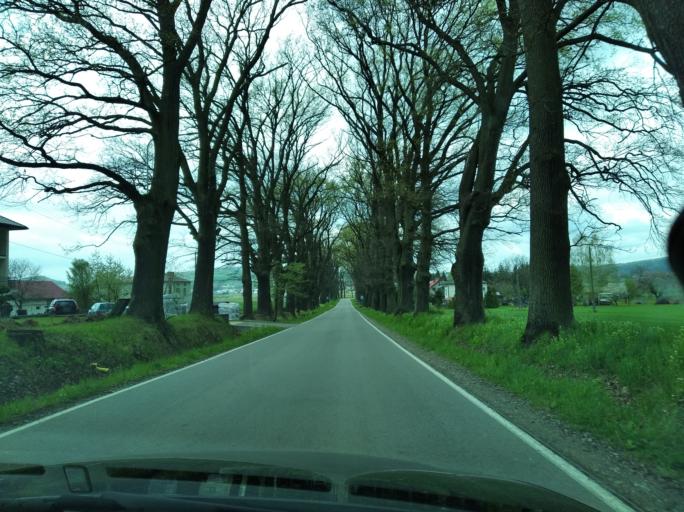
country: PL
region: Subcarpathian Voivodeship
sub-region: Powiat brzozowski
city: Turze Pole
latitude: 49.6456
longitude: 21.9980
